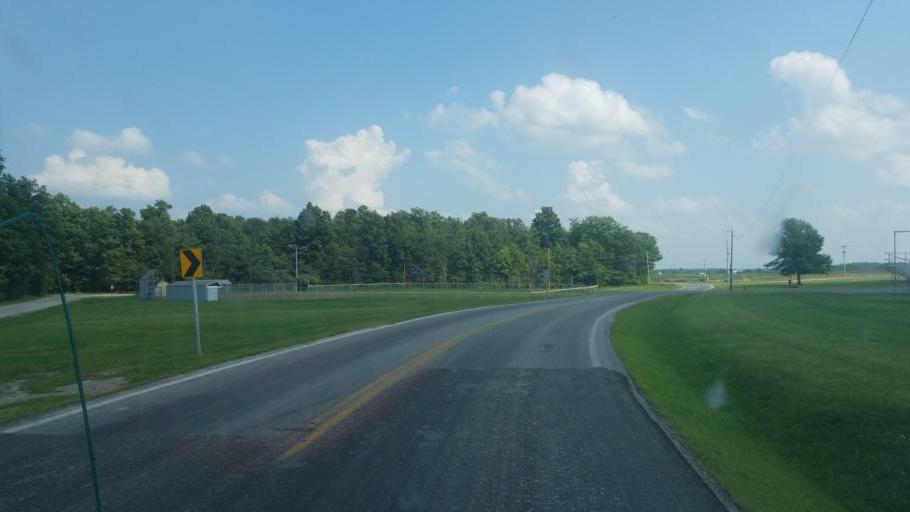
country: US
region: Ohio
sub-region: Wayne County
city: West Salem
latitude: 41.0581
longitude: -82.1738
